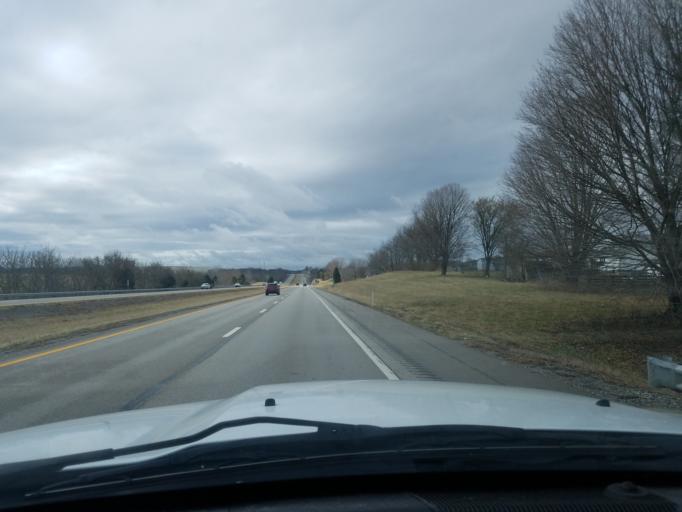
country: US
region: Kentucky
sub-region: Montgomery County
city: Mount Sterling
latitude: 38.0877
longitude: -83.9069
